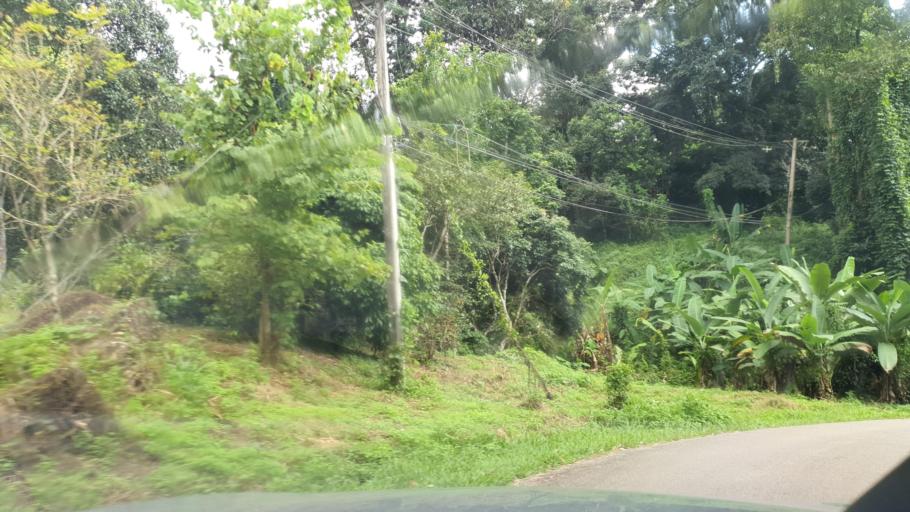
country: TH
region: Chiang Mai
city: Mae On
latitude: 18.9336
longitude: 99.3118
